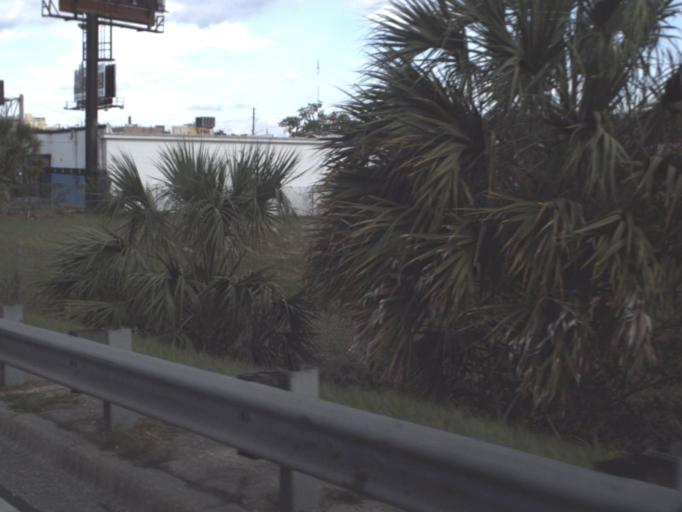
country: US
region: Florida
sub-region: Marion County
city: Ocala
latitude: 29.1870
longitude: -82.1414
